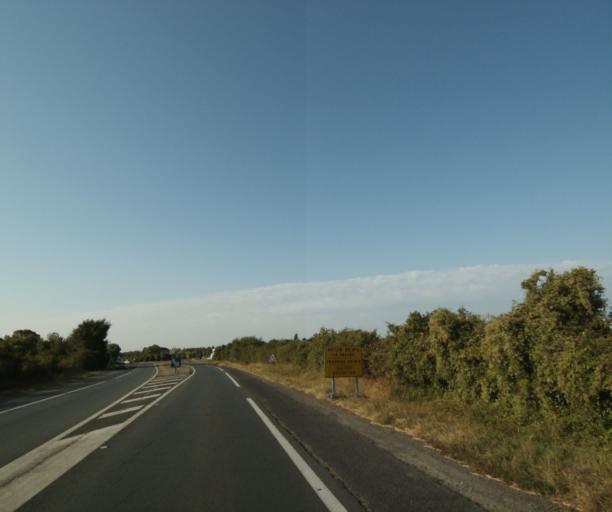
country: FR
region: Poitou-Charentes
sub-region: Departement de la Charente-Maritime
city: Saint-Hippolyte
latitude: 45.9189
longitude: -0.8858
